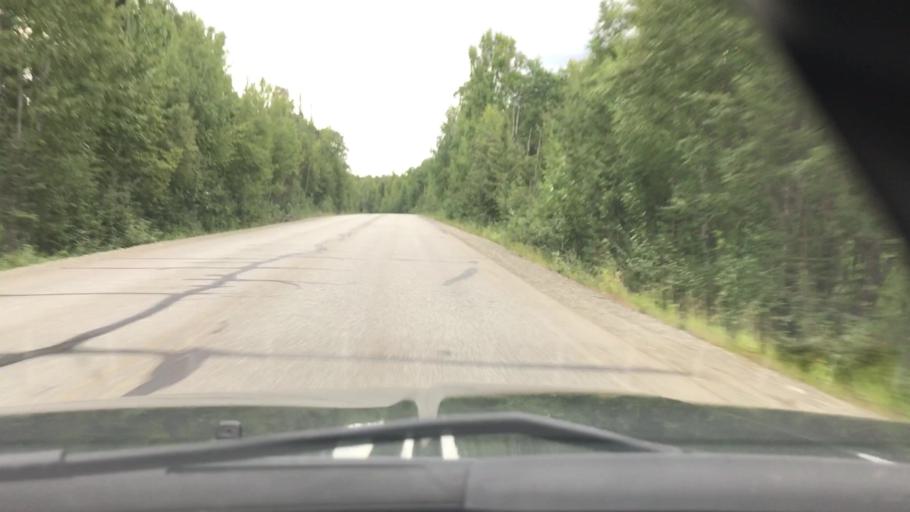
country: US
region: Alaska
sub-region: Matanuska-Susitna Borough
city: Willow
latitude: 61.7588
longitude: -150.1151
